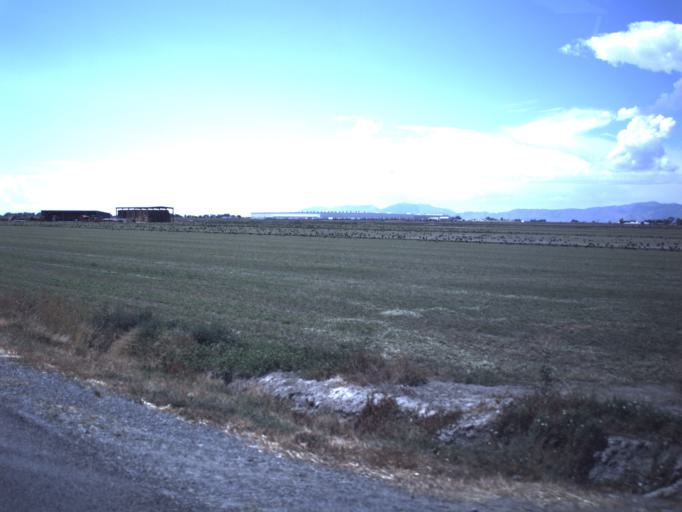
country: US
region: Utah
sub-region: Box Elder County
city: Honeyville
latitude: 41.5742
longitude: -112.1297
